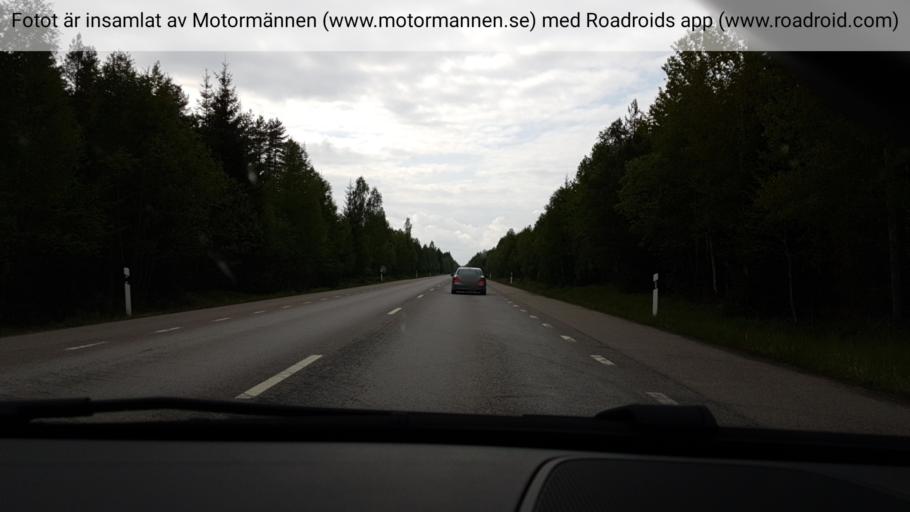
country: SE
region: Uppsala
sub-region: Osthammars Kommun
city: Gimo
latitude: 60.1641
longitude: 18.1017
